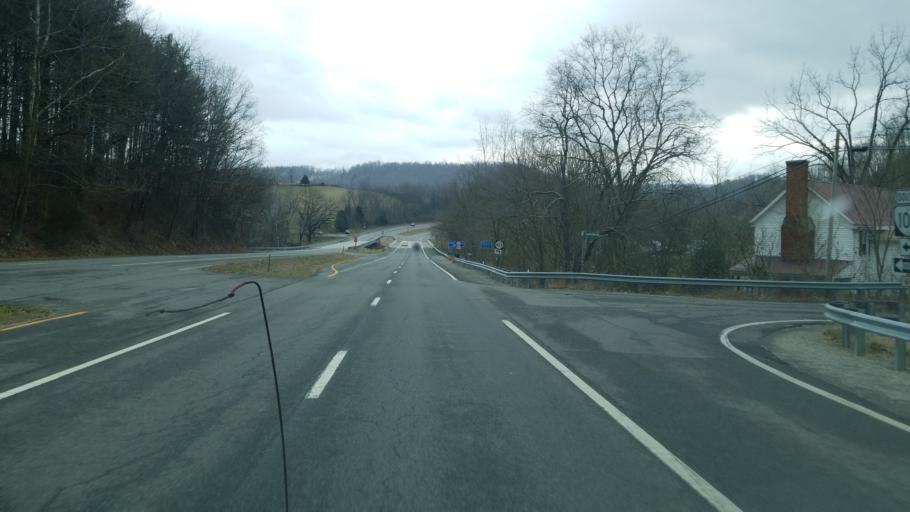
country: US
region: Virginia
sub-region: Giles County
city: Pearisburg
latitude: 37.2681
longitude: -80.7141
